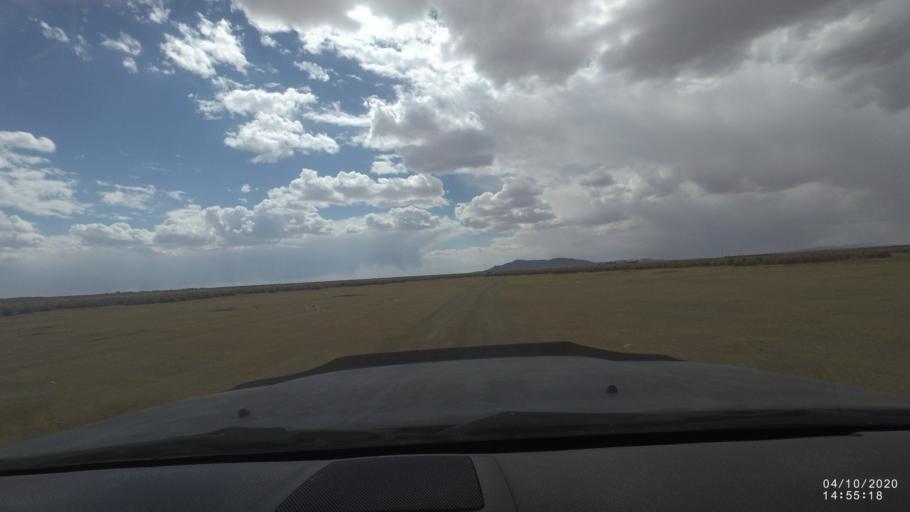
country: BO
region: Oruro
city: Poopo
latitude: -18.6846
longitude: -67.5120
